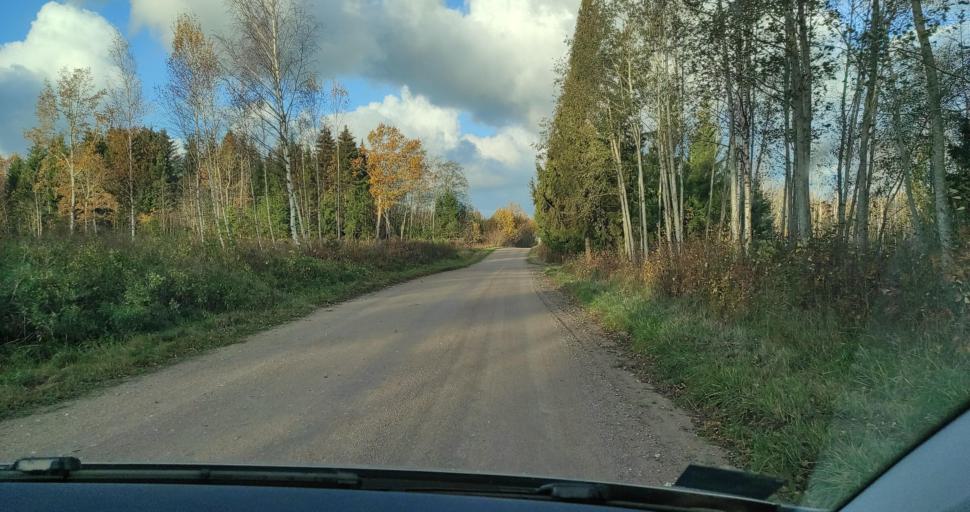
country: LV
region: Alsunga
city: Alsunga
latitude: 56.9488
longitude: 21.6351
